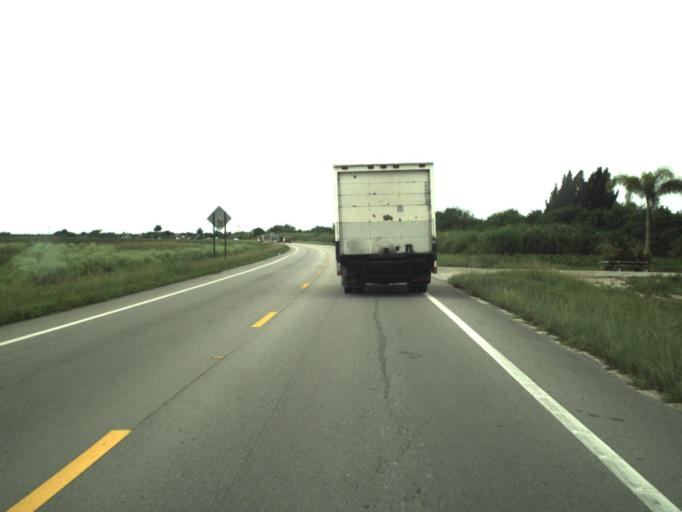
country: US
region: Florida
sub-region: Miami-Dade County
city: The Hammocks
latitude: 25.6779
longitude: -80.4806
